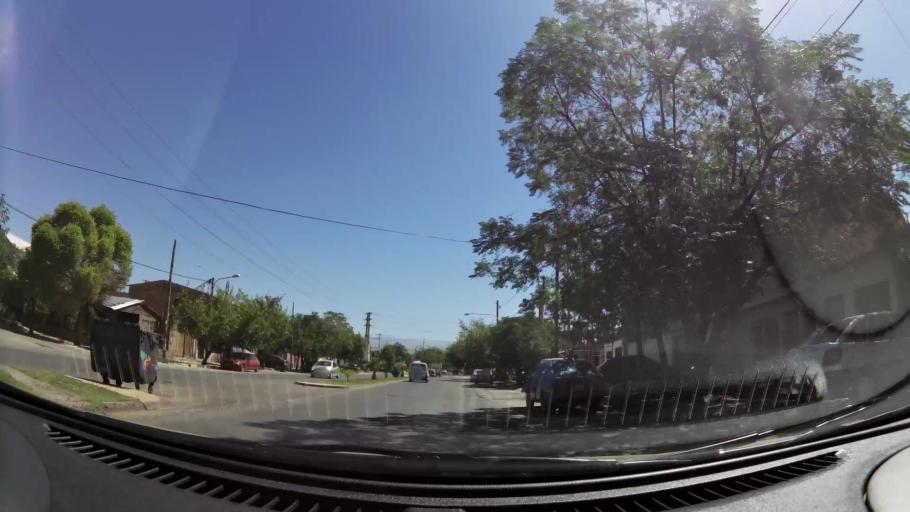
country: AR
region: Mendoza
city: Villa Nueva
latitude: -32.8806
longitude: -68.8015
